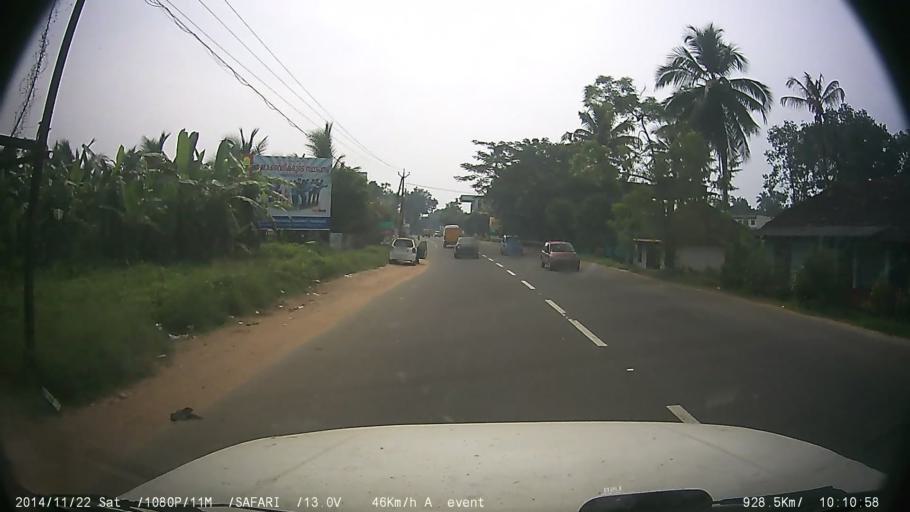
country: IN
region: Kerala
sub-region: Ernakulam
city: Muvattupula
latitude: 10.0256
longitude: 76.5558
